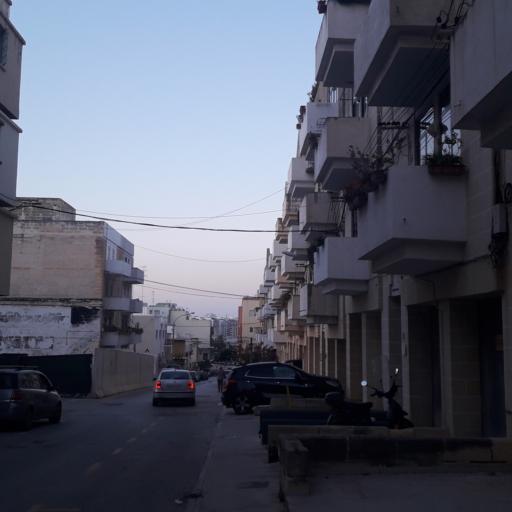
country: MT
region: Ta' Xbiex
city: Ta' Xbiex
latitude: 35.9001
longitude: 14.4926
